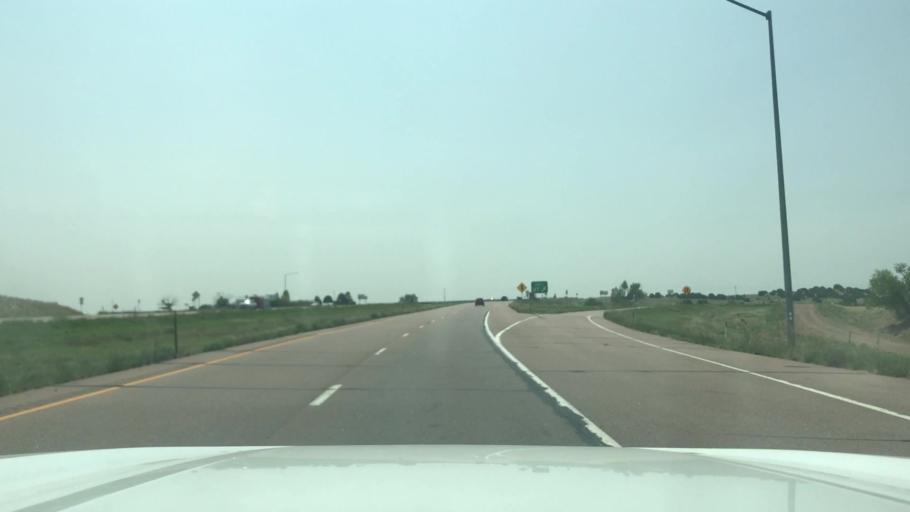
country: US
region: Colorado
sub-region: Pueblo County
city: Pueblo
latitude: 38.1176
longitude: -104.6721
